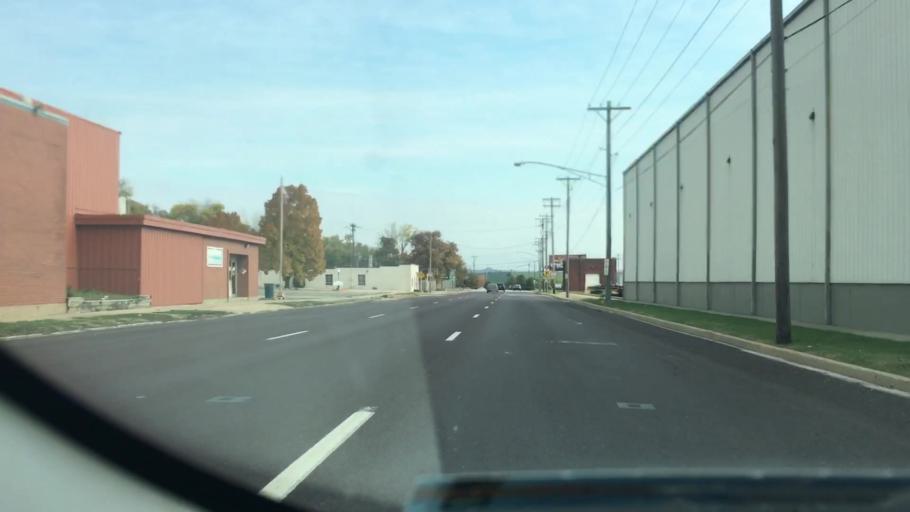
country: US
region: Illinois
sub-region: Peoria County
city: North Peoria
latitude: 40.7051
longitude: -89.5685
